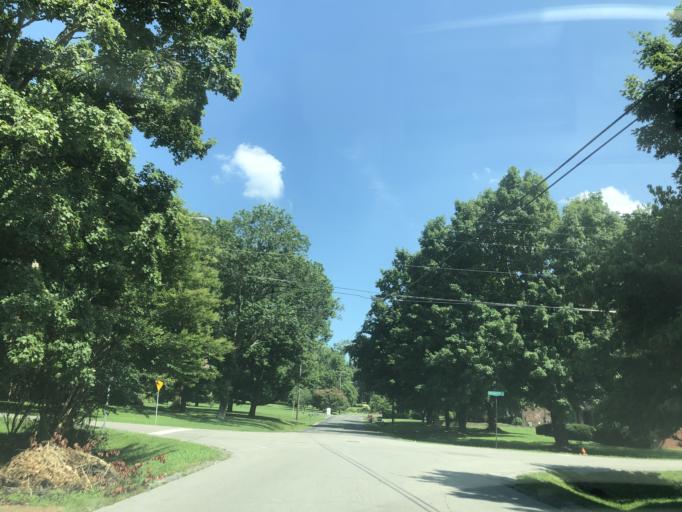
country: US
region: Tennessee
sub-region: Davidson County
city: Lakewood
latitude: 36.1811
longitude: -86.6711
